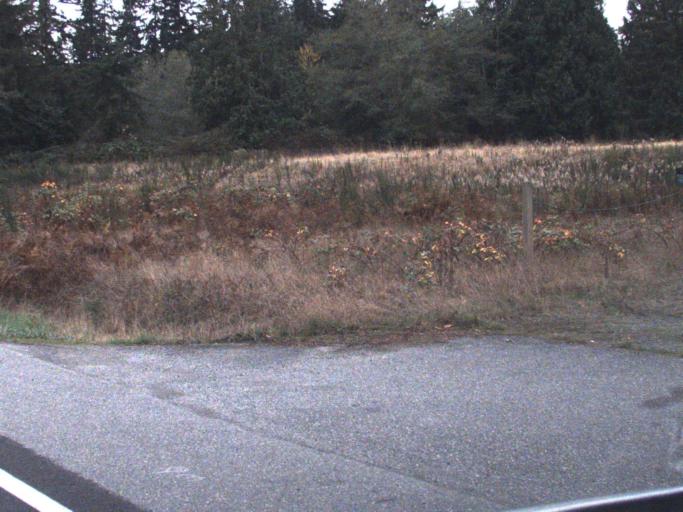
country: US
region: Washington
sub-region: Island County
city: Camano
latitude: 48.0972
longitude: -122.5725
